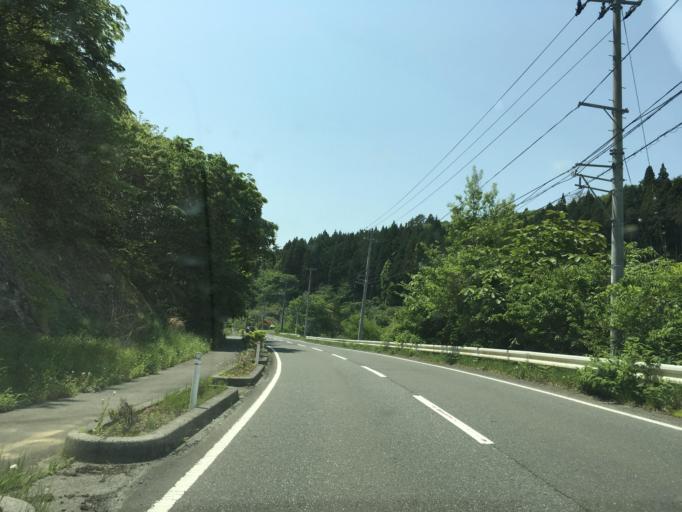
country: JP
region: Iwate
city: Ofunato
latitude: 38.8625
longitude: 141.5257
